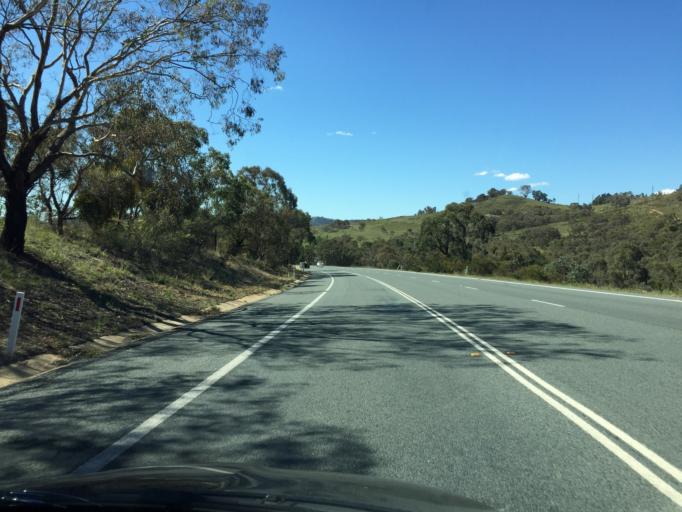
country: AU
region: Australian Capital Territory
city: Macarthur
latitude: -35.4455
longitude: 149.1307
